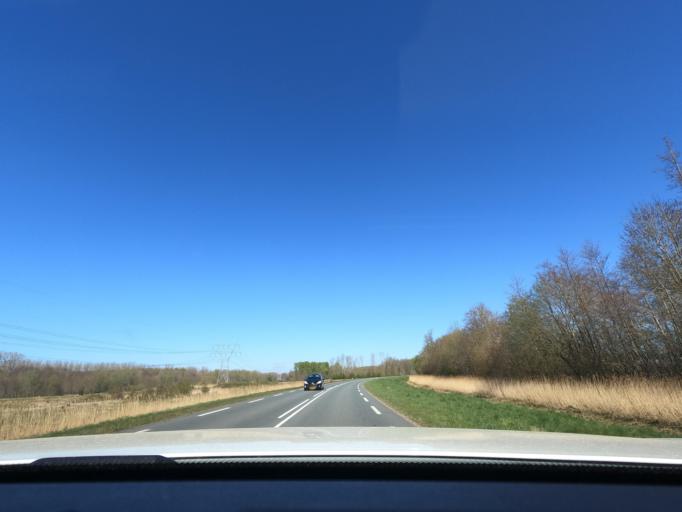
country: NL
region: Gelderland
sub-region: Gemeente Harderwijk
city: Harderwijk
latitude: 52.3806
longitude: 5.6190
